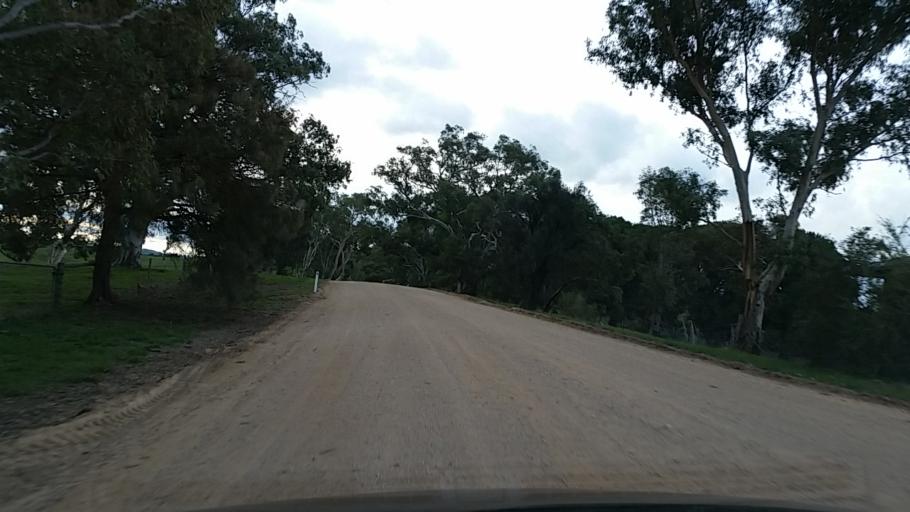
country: AU
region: South Australia
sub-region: Adelaide Hills
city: Birdwood
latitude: -34.9393
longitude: 139.0133
